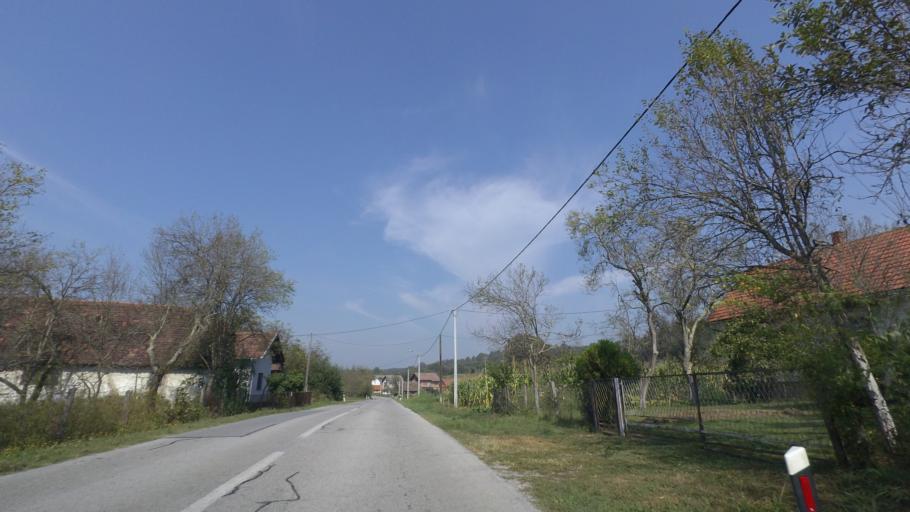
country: BA
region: Republika Srpska
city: Knezica
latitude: 45.2066
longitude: 16.6810
